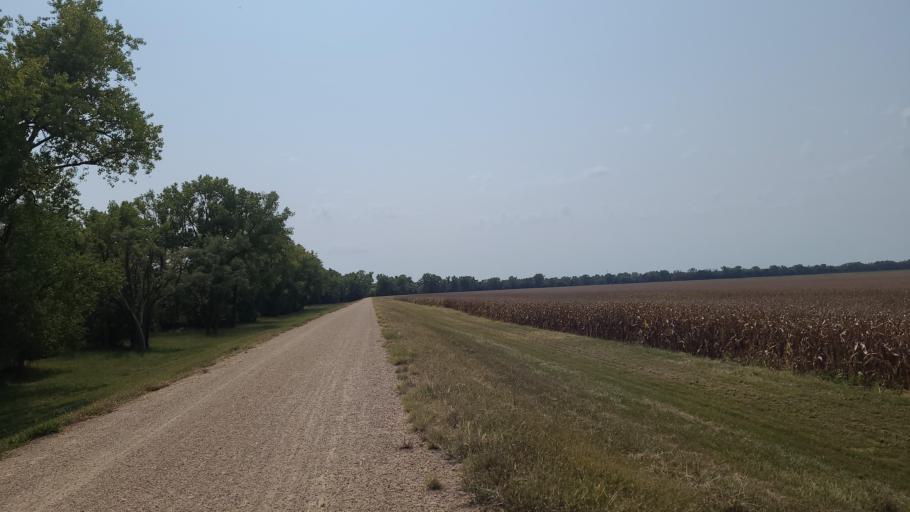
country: US
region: Kansas
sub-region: Douglas County
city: Lawrence
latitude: 38.9780
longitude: -95.1704
